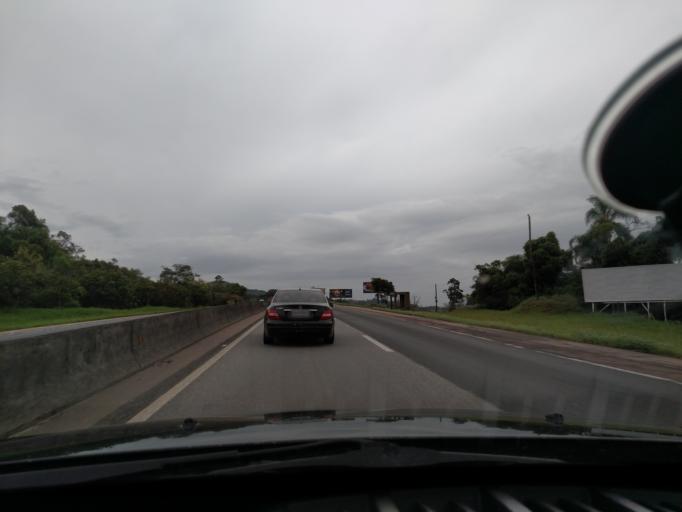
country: BR
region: Santa Catarina
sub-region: Tijucas
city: Tijucas
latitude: -27.3239
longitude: -48.6273
